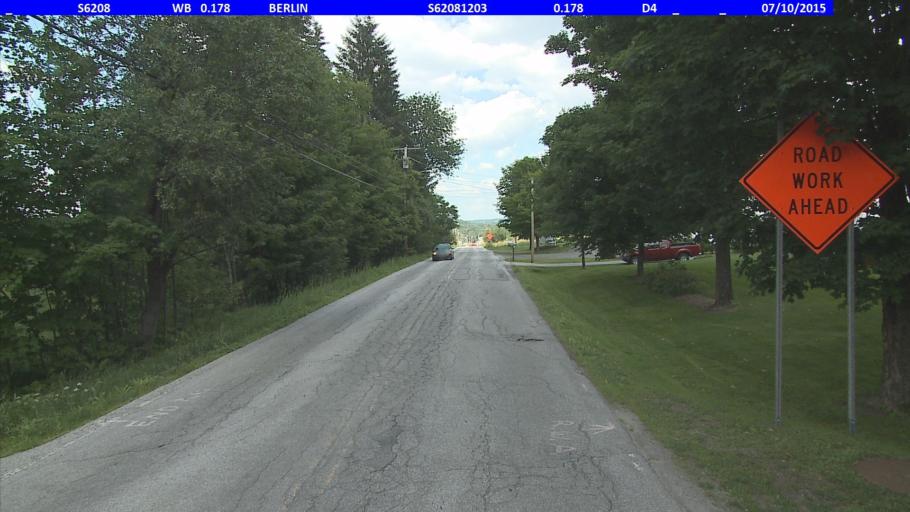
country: US
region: Vermont
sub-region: Washington County
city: Montpelier
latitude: 44.2076
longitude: -72.5775
